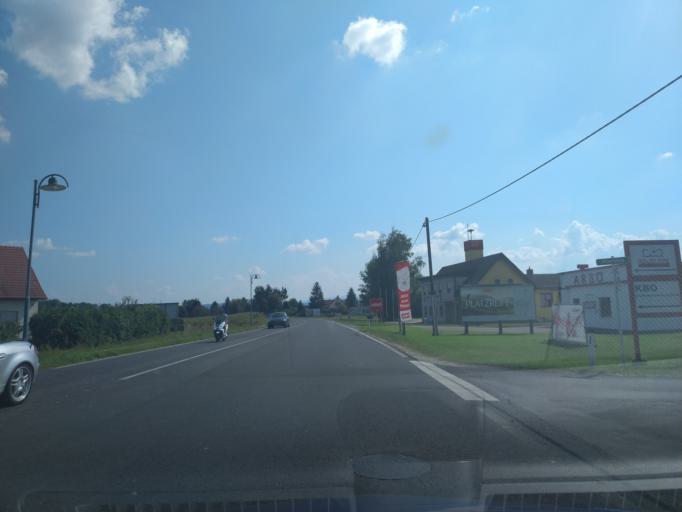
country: AT
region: Styria
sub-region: Politischer Bezirk Leibnitz
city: Gabersdorf
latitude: 46.7823
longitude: 15.5649
